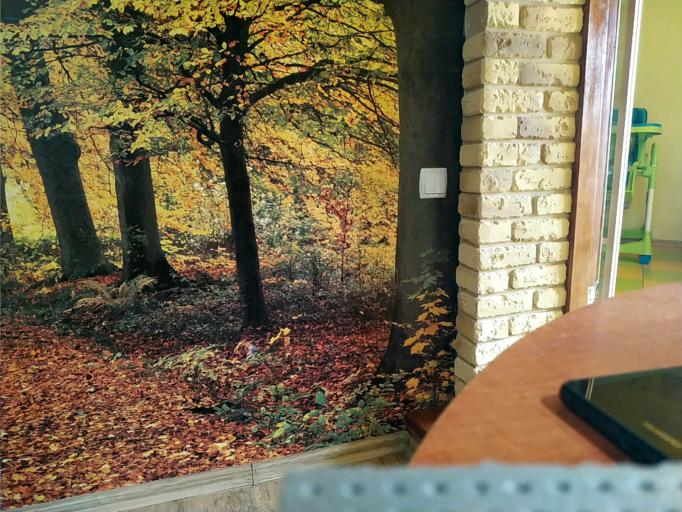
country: RU
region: Tverskaya
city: Kalashnikovo
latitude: 57.2828
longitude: 35.1147
